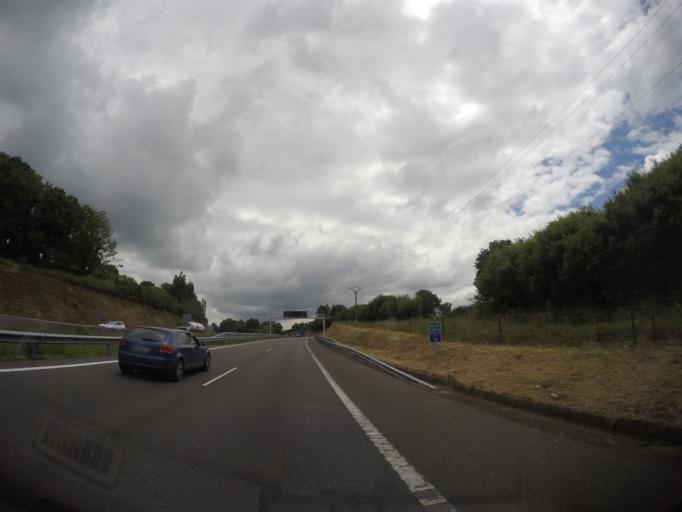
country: ES
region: Galicia
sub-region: Provincia da Coruna
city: Oleiros
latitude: 43.2919
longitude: -8.2968
